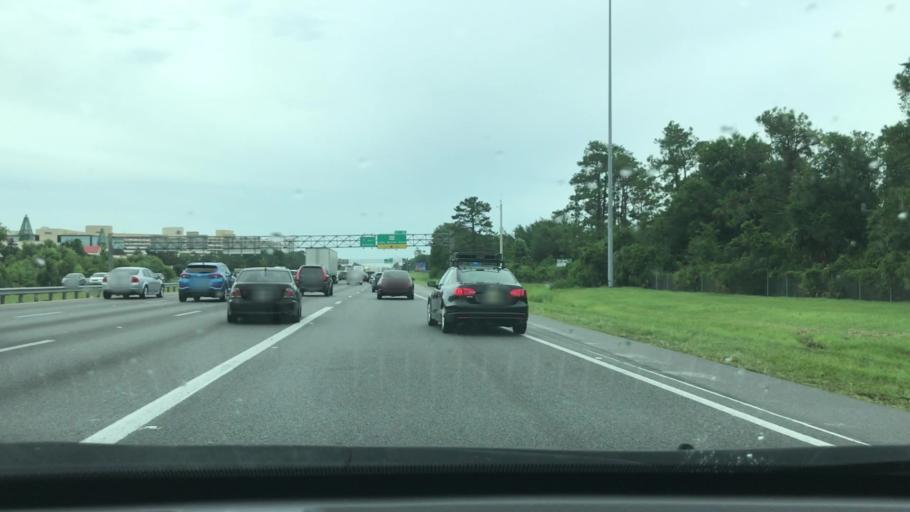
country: US
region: Florida
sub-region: Osceola County
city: Celebration
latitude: 28.3664
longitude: -81.5134
